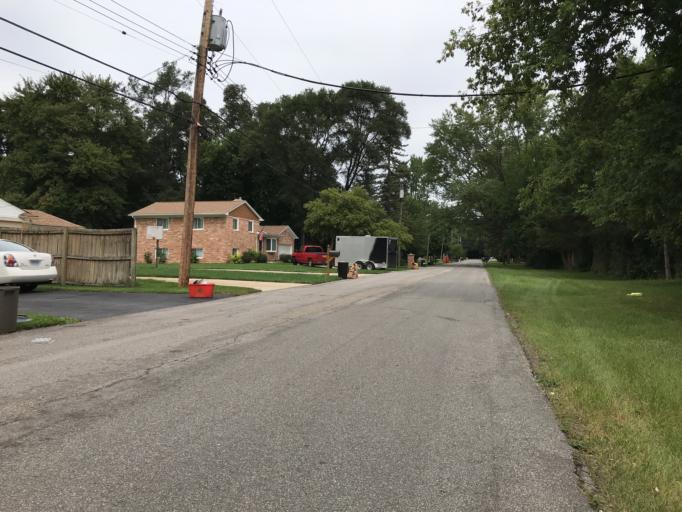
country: US
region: Michigan
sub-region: Oakland County
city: Bingham Farms
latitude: 42.4578
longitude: -83.2819
